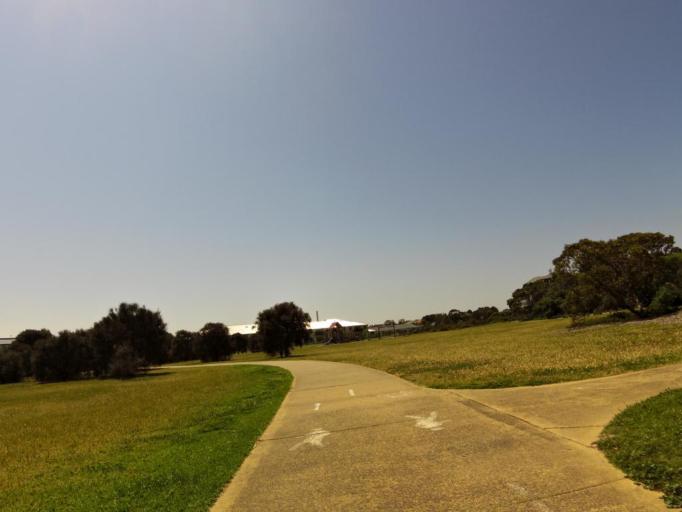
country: AU
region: Victoria
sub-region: Hobsons Bay
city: Williamstown North
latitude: -37.8615
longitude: 144.8763
